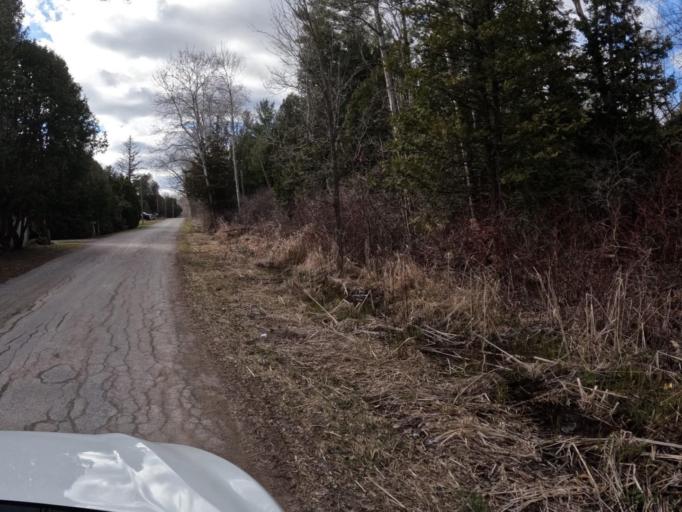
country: CA
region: Ontario
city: Norfolk County
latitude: 42.7659
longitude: -80.3061
